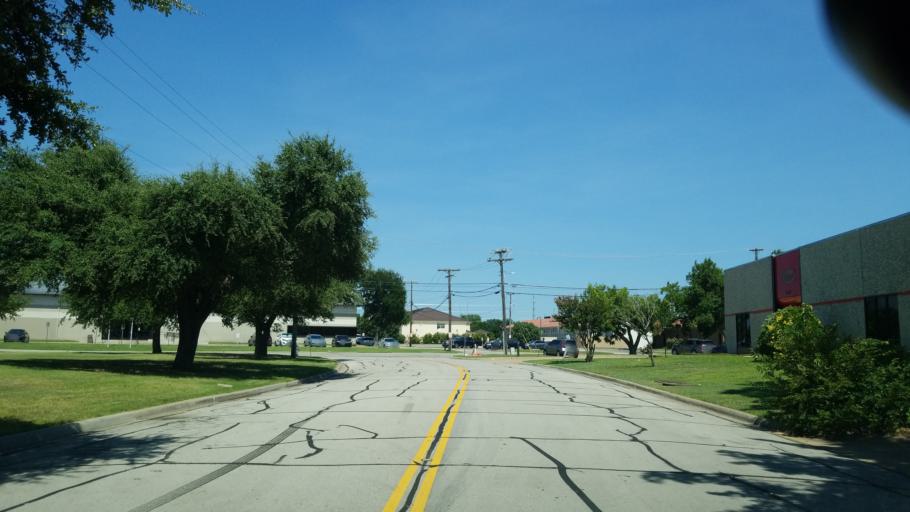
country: US
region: Texas
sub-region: Dallas County
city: Farmers Branch
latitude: 32.9239
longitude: -96.9038
